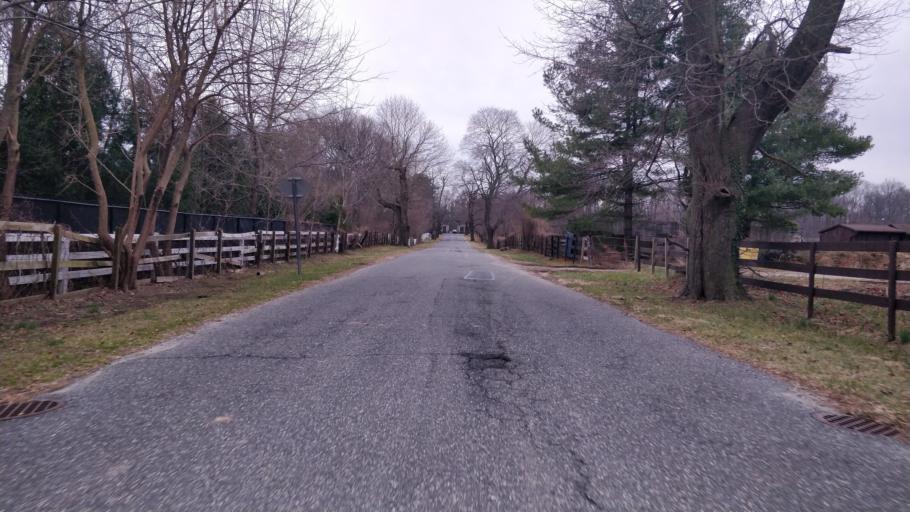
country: US
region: New York
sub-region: Nassau County
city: Old Westbury
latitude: 40.7831
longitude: -73.5788
